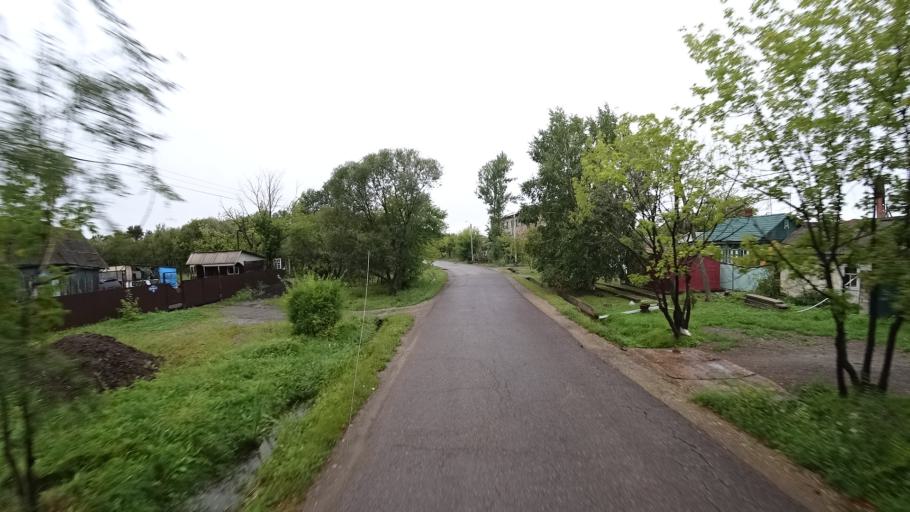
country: RU
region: Primorskiy
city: Monastyrishche
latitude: 44.2026
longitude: 132.4600
